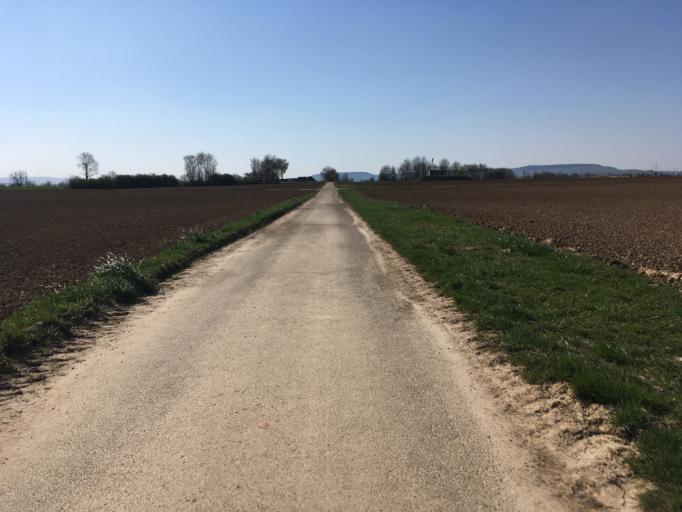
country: DE
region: Baden-Wuerttemberg
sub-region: Regierungsbezirk Stuttgart
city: Flein
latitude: 49.1082
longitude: 9.1914
